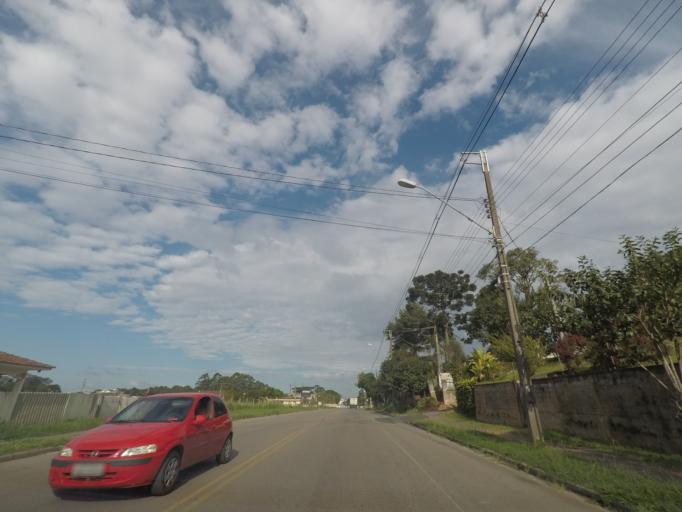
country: BR
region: Parana
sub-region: Sao Jose Dos Pinhais
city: Sao Jose dos Pinhais
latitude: -25.5726
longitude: -49.2791
